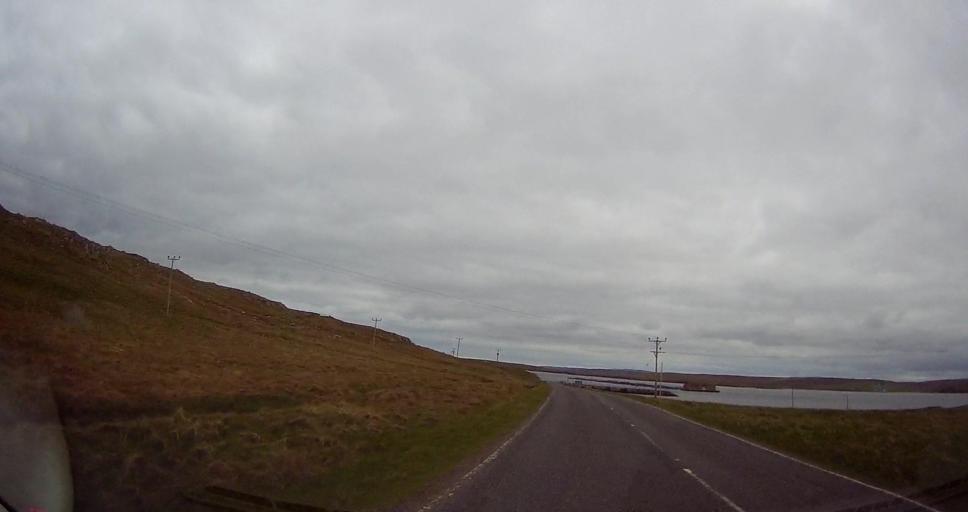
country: GB
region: Scotland
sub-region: Shetland Islands
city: Shetland
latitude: 60.6867
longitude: -0.9640
